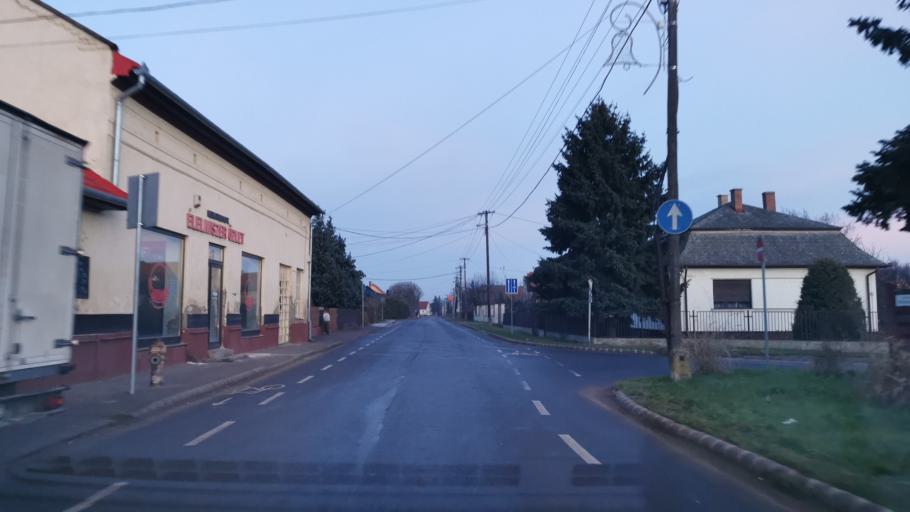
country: HU
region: Hajdu-Bihar
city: Hajduboszormeny
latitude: 47.5936
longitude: 21.5628
